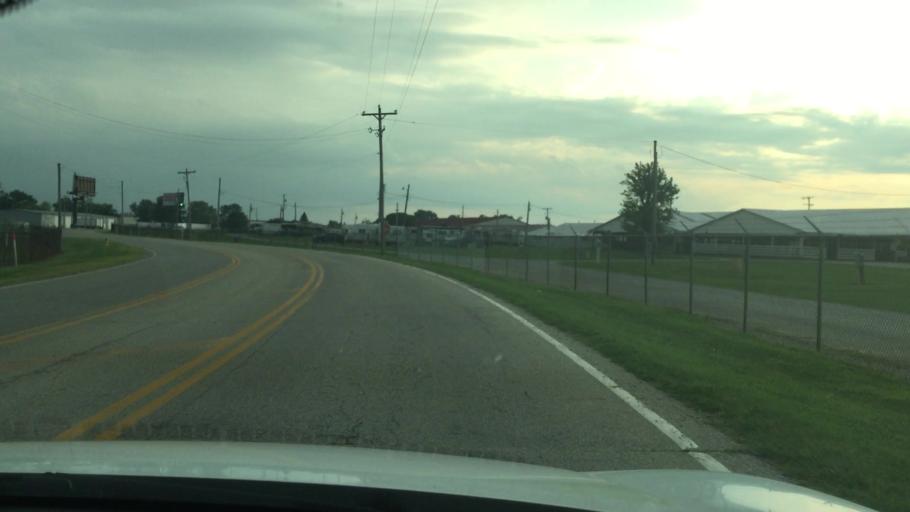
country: US
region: Ohio
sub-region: Clark County
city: Springfield
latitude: 39.8965
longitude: -83.7281
